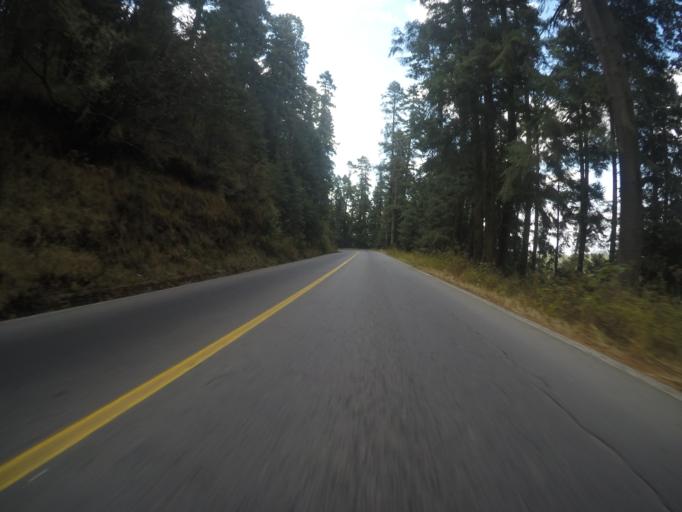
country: MX
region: Mexico
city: Cerro La Calera
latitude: 19.1816
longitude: -99.8032
